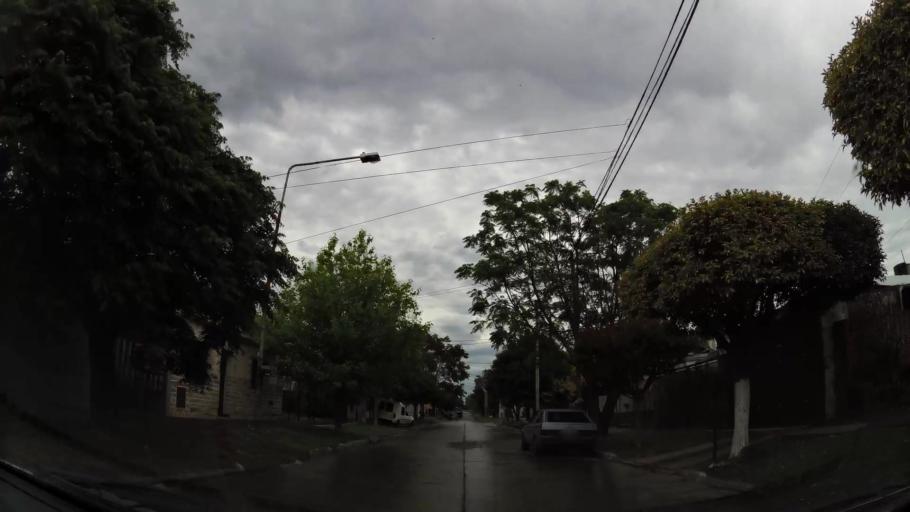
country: AR
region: Buenos Aires
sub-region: Partido de Quilmes
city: Quilmes
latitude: -34.7648
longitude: -58.2281
